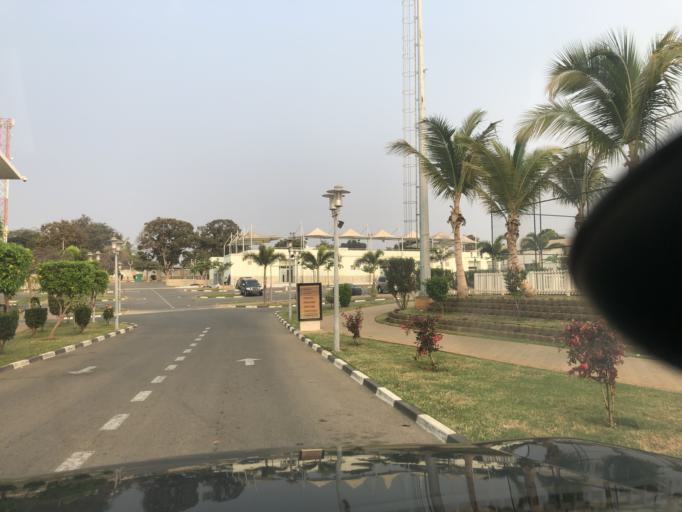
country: AO
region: Luanda
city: Luanda
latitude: -8.8893
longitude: 13.1812
